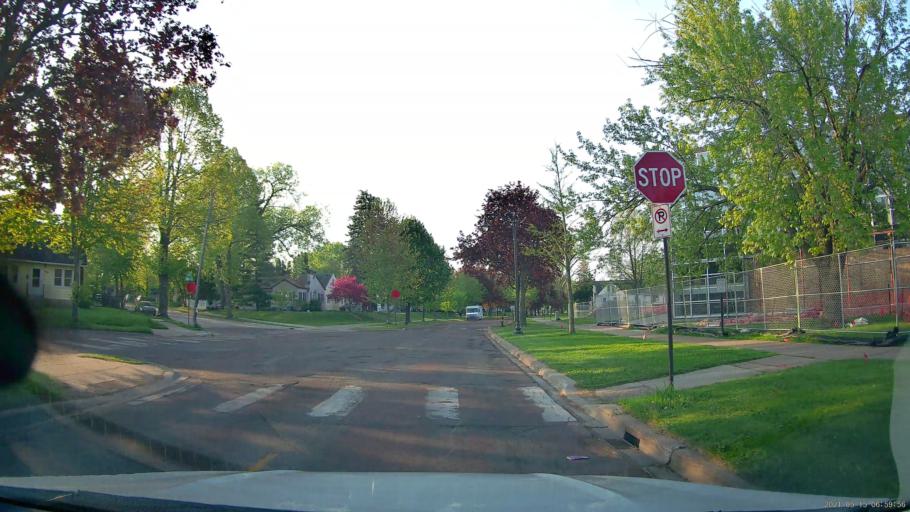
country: US
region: Minnesota
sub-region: Hennepin County
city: Saint Anthony
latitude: 45.0225
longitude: -93.2336
